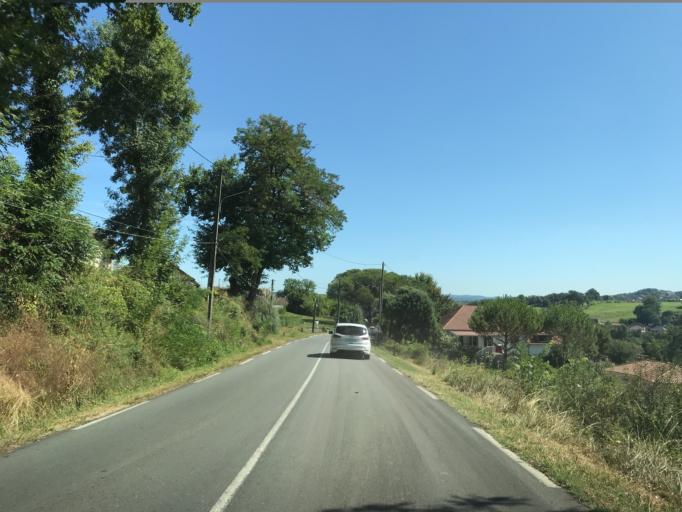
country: FR
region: Limousin
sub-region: Departement de la Correze
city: Larche
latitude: 45.1162
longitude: 1.4079
